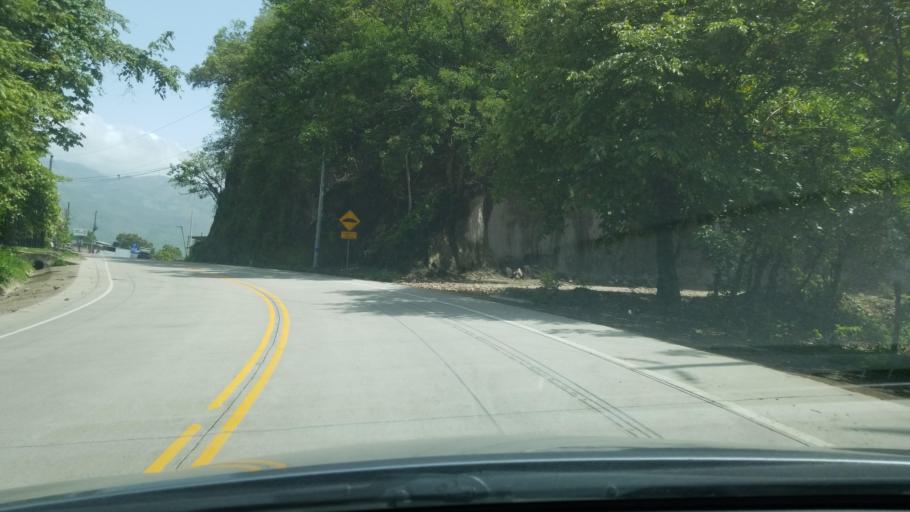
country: HN
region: Copan
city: Florida
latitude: 15.0229
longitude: -88.8314
